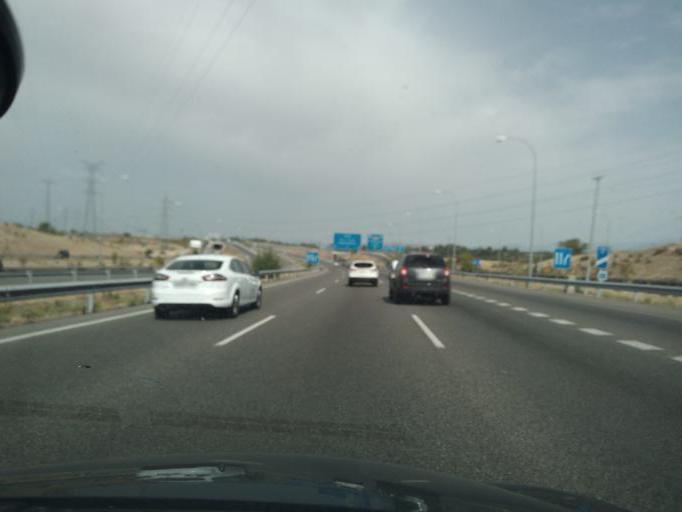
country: ES
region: Madrid
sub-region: Provincia de Madrid
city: Las Tablas
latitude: 40.5175
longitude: -3.6730
